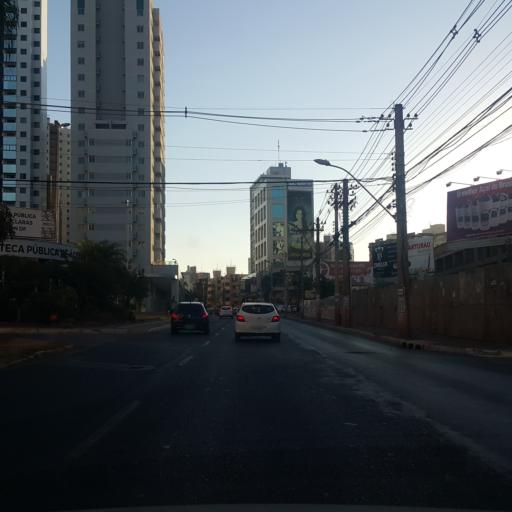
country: BR
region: Federal District
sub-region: Brasilia
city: Brasilia
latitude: -15.8340
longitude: -48.0127
